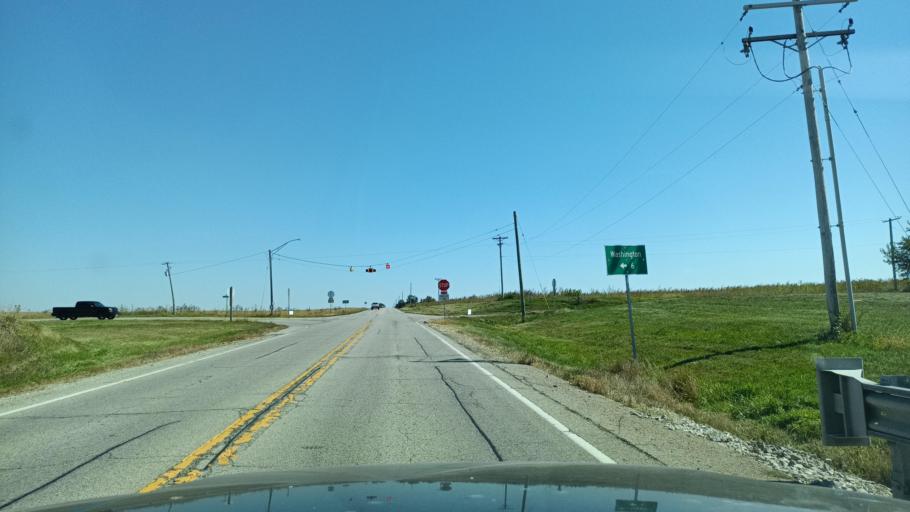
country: US
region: Illinois
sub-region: Tazewell County
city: Morton
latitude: 40.6139
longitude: -89.4041
